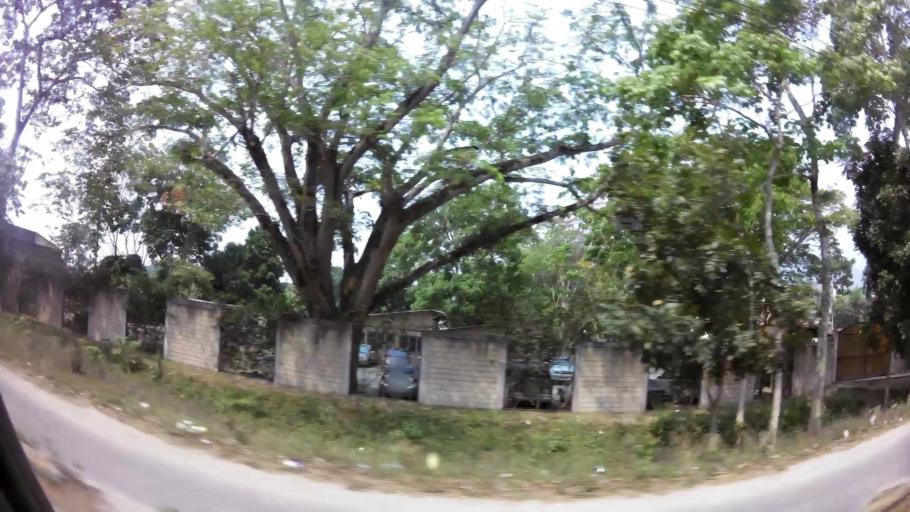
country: HN
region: Cortes
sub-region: San Pedro Sula
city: Pena Blanca
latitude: 15.5610
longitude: -88.0193
